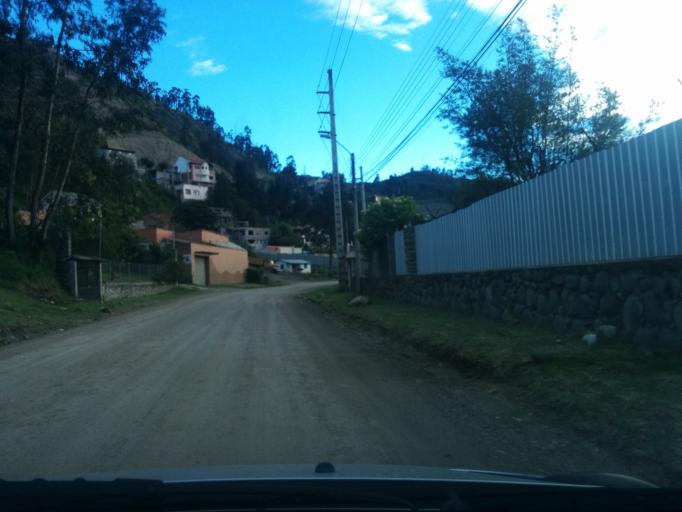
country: EC
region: Azuay
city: Cuenca
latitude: -2.8793
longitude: -78.9458
